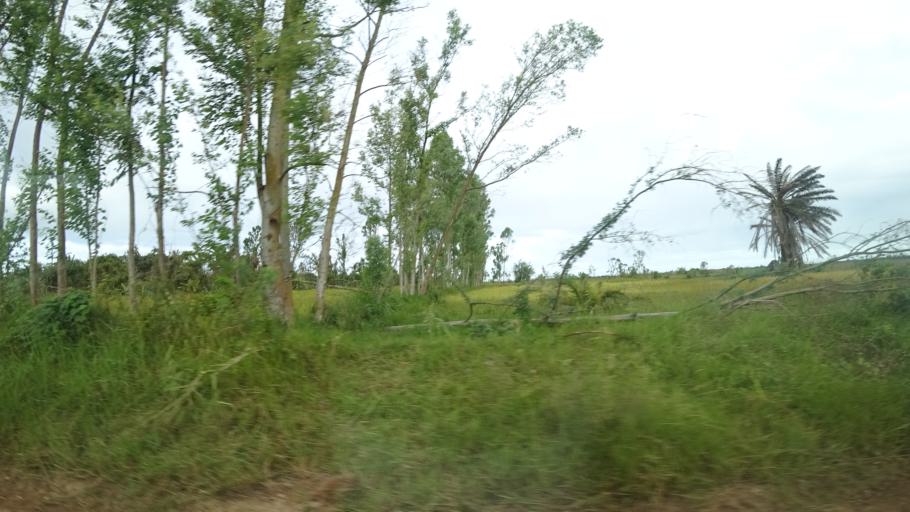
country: MZ
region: Sofala
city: Beira
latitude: -19.7186
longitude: 35.0032
